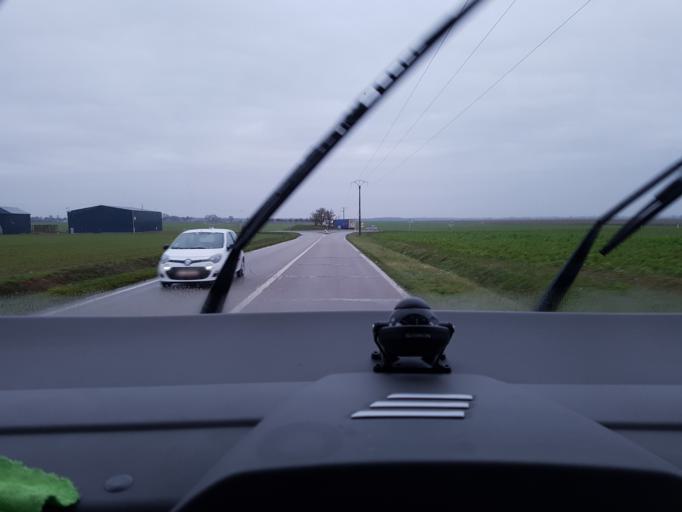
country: FR
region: Haute-Normandie
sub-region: Departement de l'Eure
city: Le Neubourg
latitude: 49.1564
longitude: 0.9923
